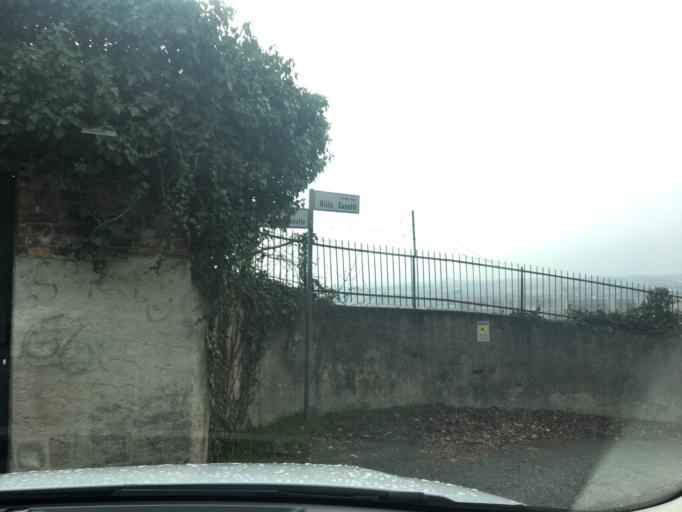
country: IT
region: Piedmont
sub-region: Provincia di Torino
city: Moncalieri
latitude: 45.0286
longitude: 7.6807
